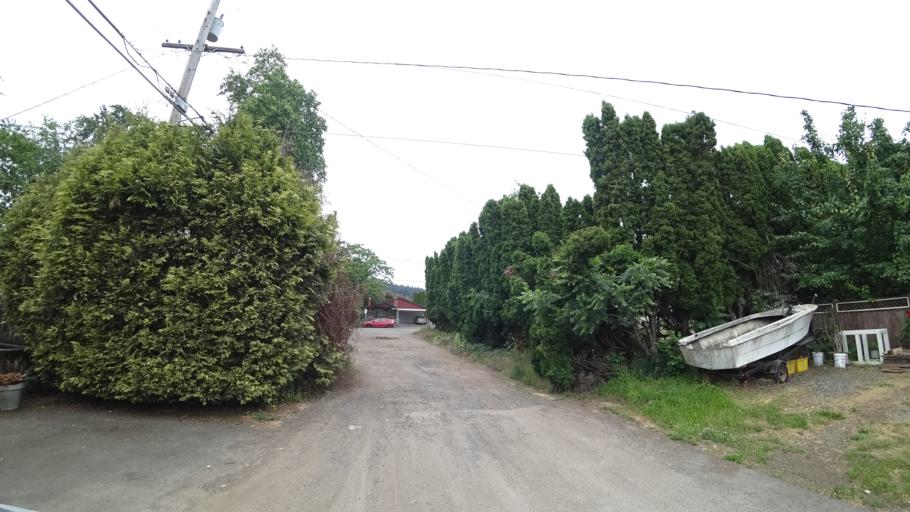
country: US
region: Oregon
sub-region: Multnomah County
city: Lents
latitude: 45.5136
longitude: -122.5766
